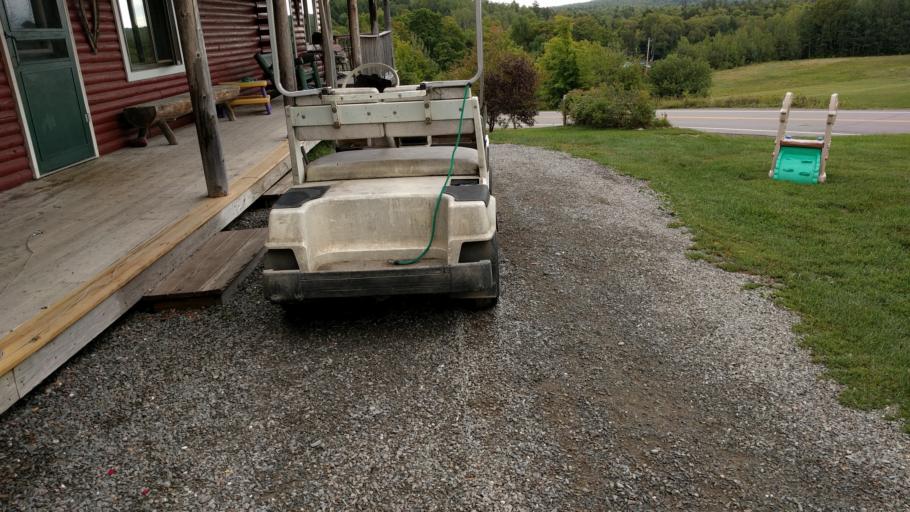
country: US
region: Maine
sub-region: Penobscot County
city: Patten
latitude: 46.1064
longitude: -68.5592
